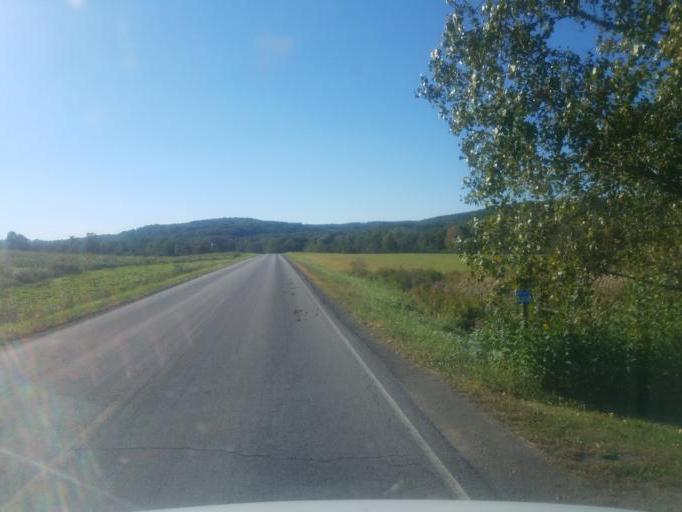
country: US
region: New York
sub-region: Allegany County
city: Cuba
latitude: 42.2755
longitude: -78.2123
